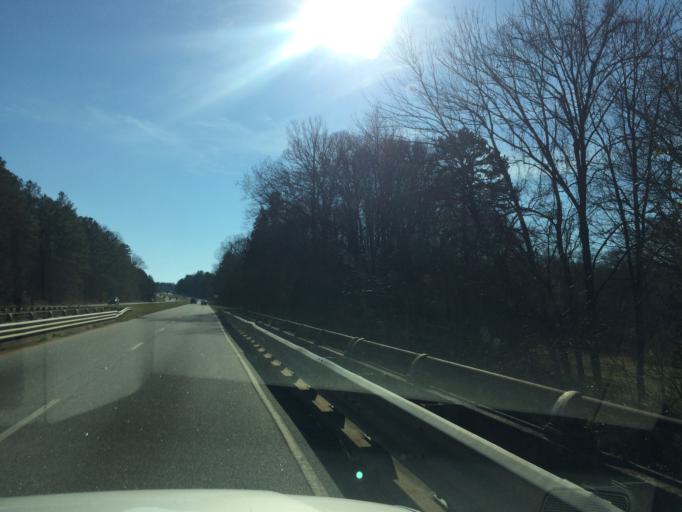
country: US
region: South Carolina
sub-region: Greenwood County
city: Greenwood
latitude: 34.2452
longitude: -82.1003
